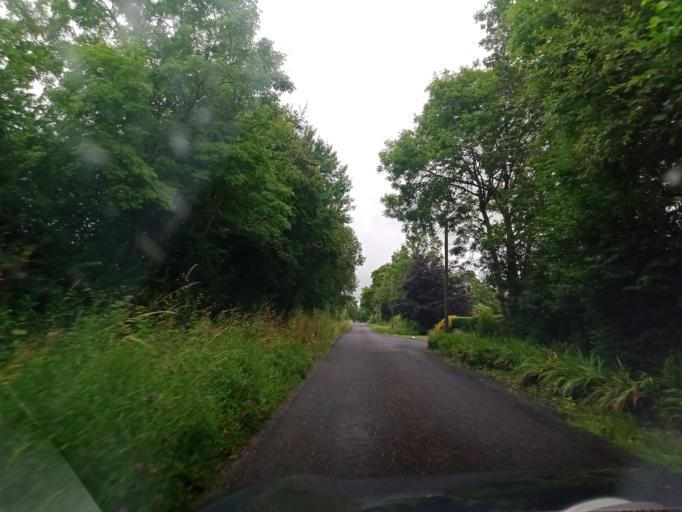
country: IE
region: Leinster
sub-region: Laois
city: Stradbally
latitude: 52.9562
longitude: -7.2147
